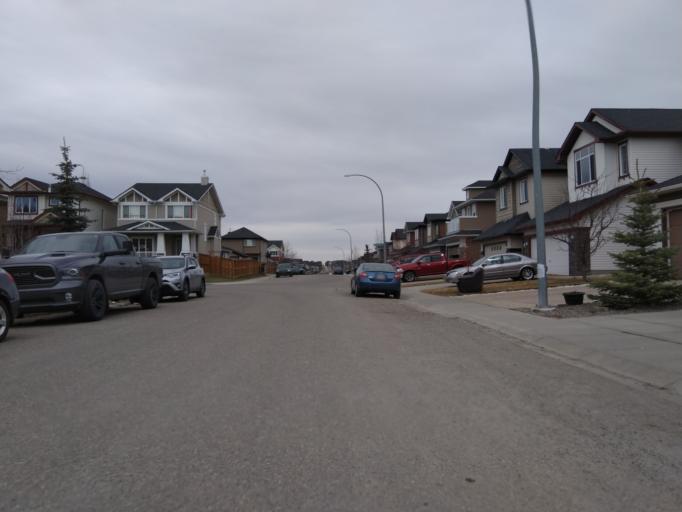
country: CA
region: Alberta
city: Calgary
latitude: 51.1695
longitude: -114.1082
